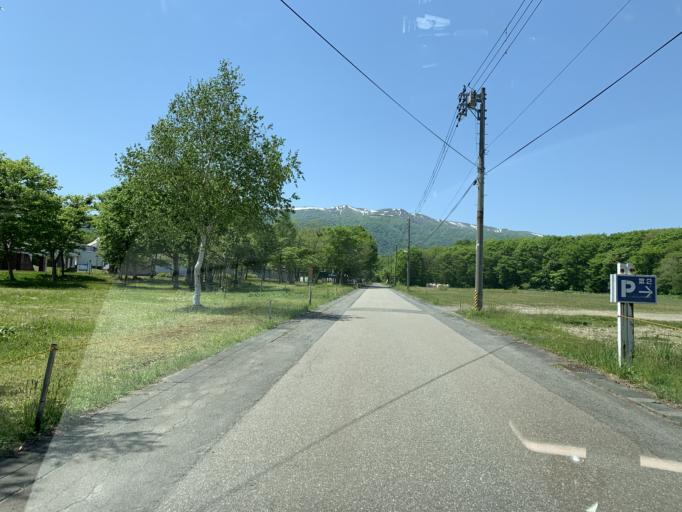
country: JP
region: Iwate
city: Shizukuishi
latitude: 39.5426
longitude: 140.8282
